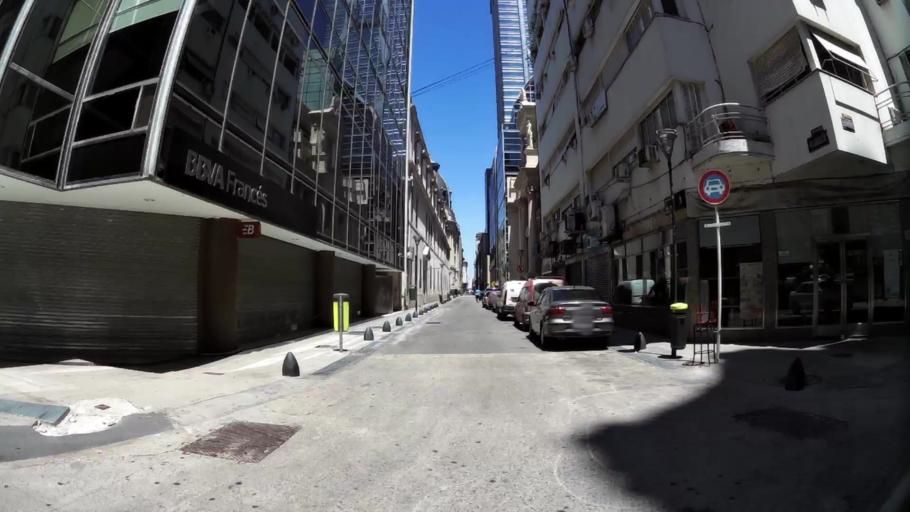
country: AR
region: Buenos Aires F.D.
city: Buenos Aires
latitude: -34.6044
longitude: -58.3724
